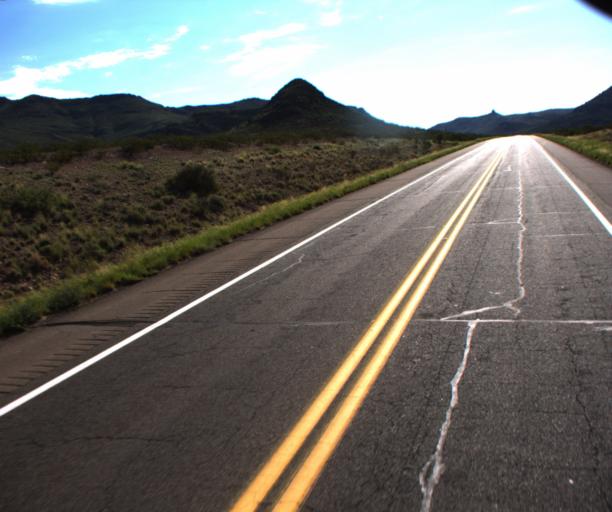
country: US
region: Arizona
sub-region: Greenlee County
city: Clifton
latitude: 32.8475
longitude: -109.3848
